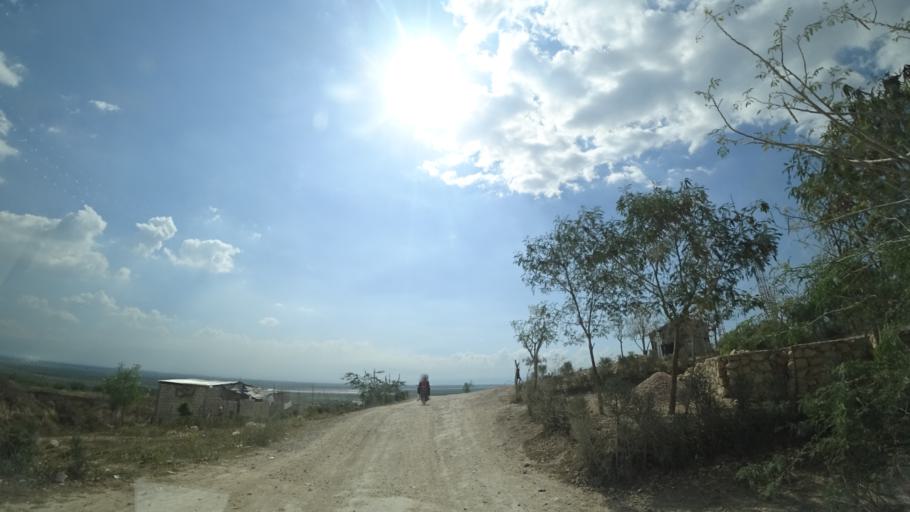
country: HT
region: Ouest
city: Cabaret
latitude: 18.6754
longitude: -72.3090
